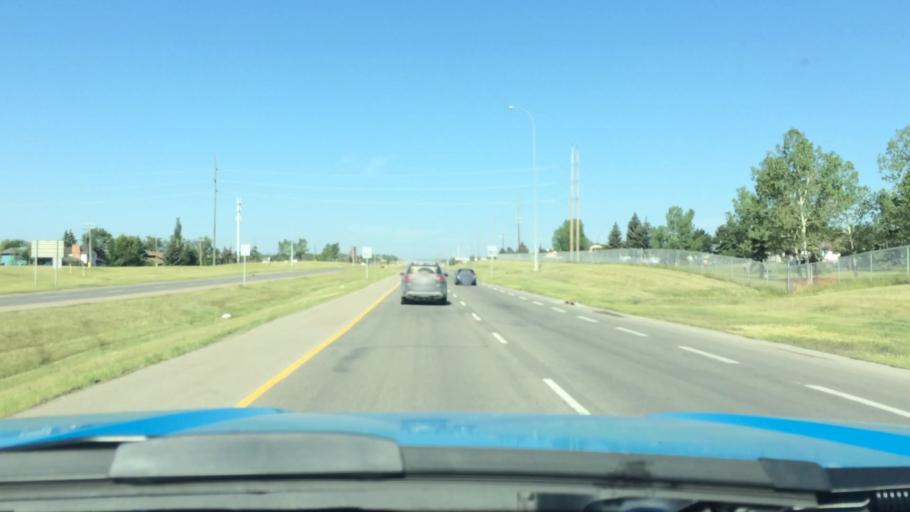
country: CA
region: Alberta
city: Chestermere
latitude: 51.0962
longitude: -113.9384
